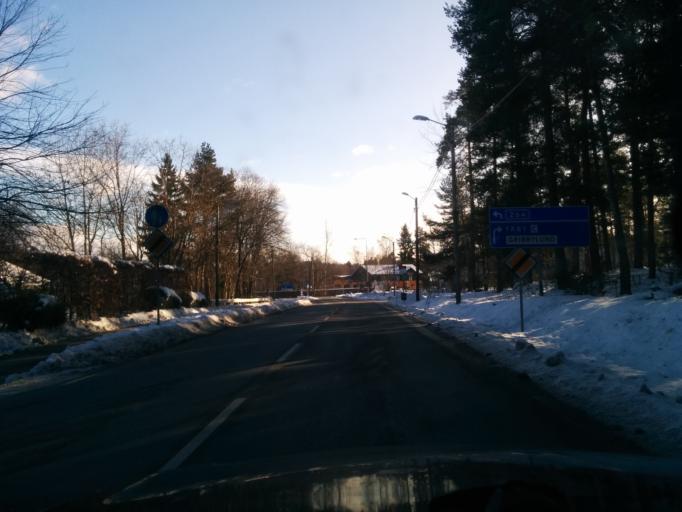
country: SE
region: Stockholm
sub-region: Taby Kommun
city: Taby
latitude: 59.4737
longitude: 18.0967
